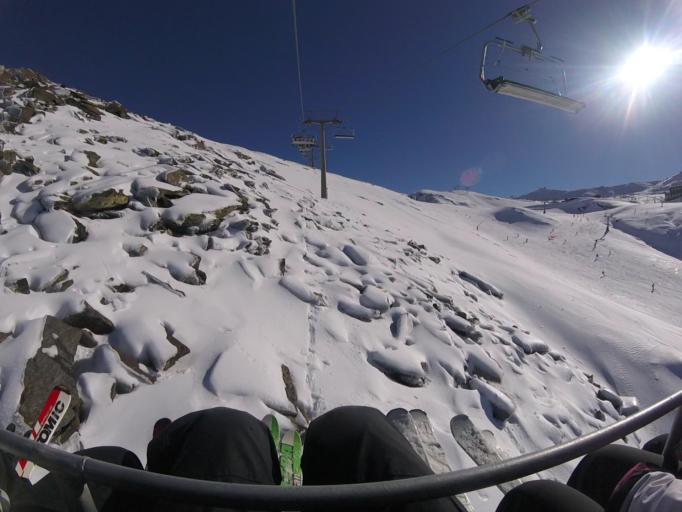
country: ES
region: Andalusia
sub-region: Provincia de Granada
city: Guejar-Sierra
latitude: 37.0747
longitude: -3.3864
